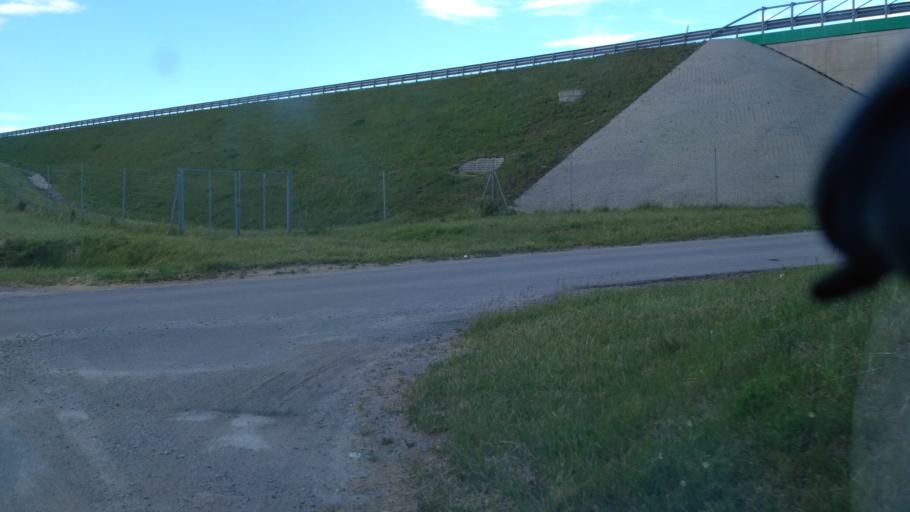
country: PL
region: Subcarpathian Voivodeship
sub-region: Powiat jaroslawski
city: Pawlosiow
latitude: 49.9527
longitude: 22.6612
